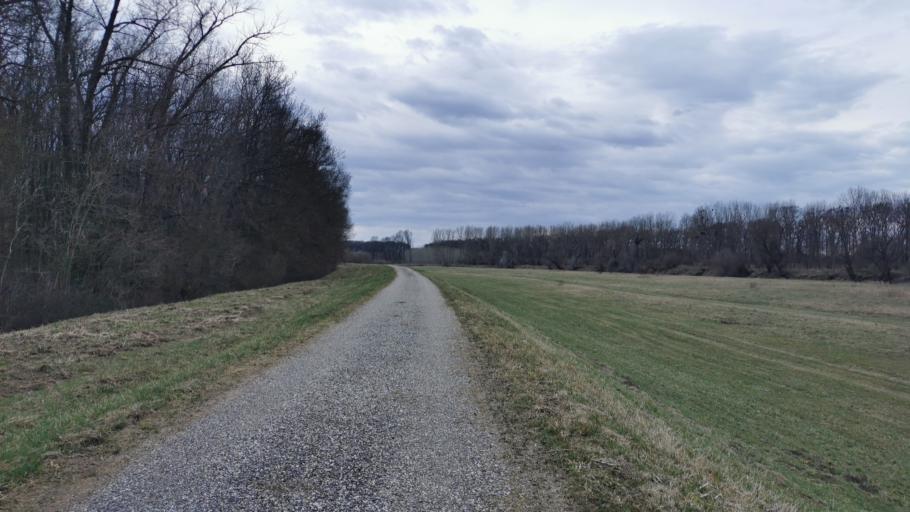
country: CZ
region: South Moravian
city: Hodonin
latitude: 48.8266
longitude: 17.1084
